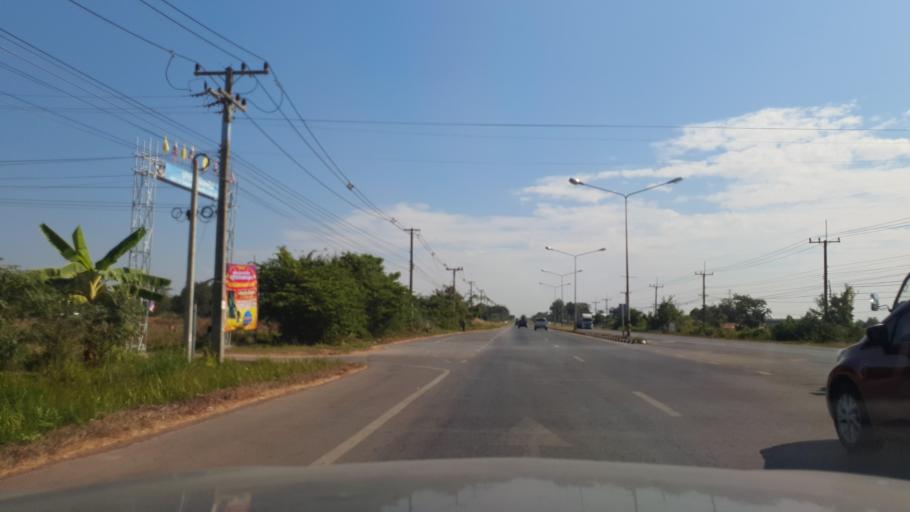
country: TH
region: Maha Sarakham
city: Chiang Yuen
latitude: 16.3729
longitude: 103.1455
